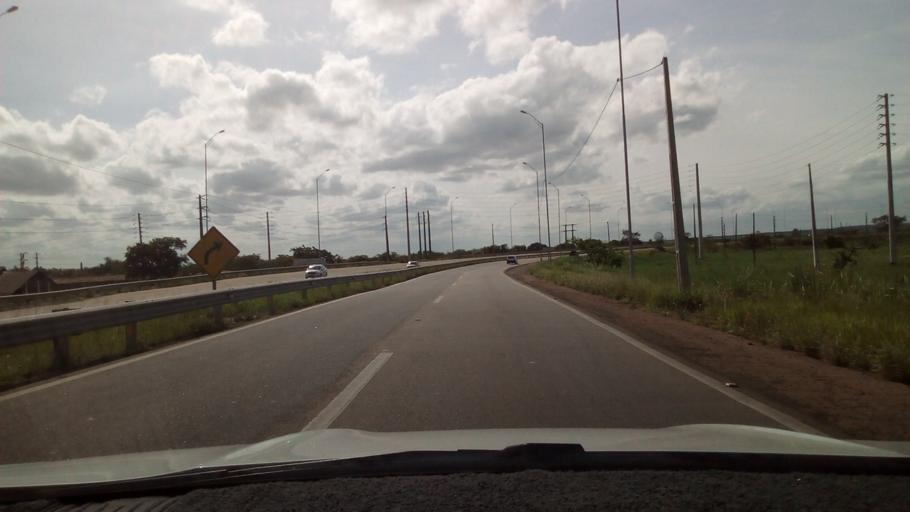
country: BR
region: Paraiba
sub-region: Santa Rita
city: Santa Rita
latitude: -7.1146
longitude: -34.9587
